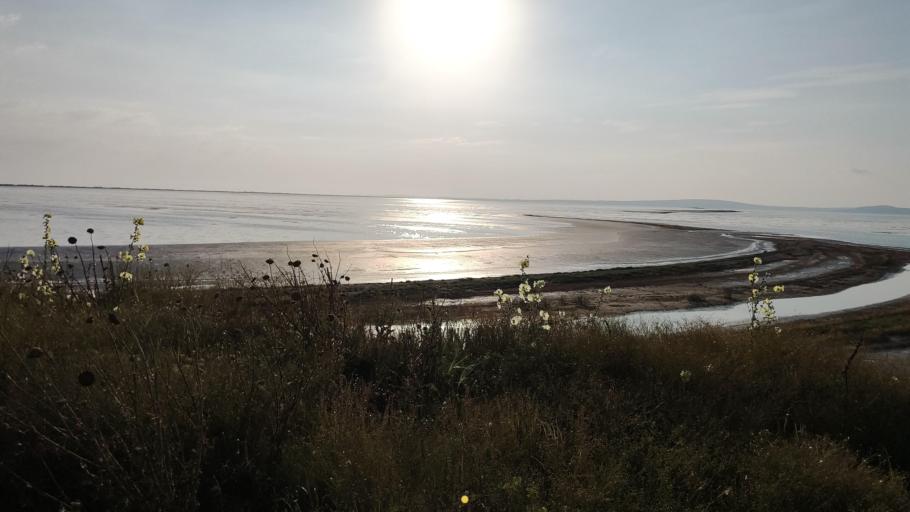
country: RU
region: Krasnodarskiy
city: Blagovetschenskaya
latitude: 45.0753
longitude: 37.0594
